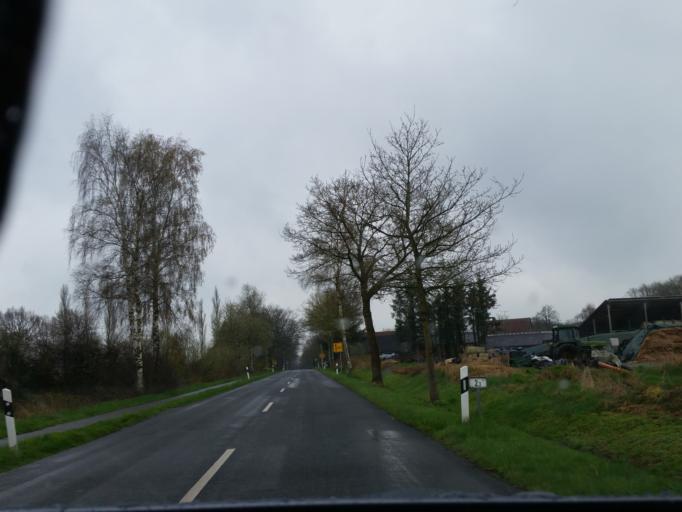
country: DE
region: Lower Saxony
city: Hipstedt
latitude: 53.4854
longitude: 8.9676
